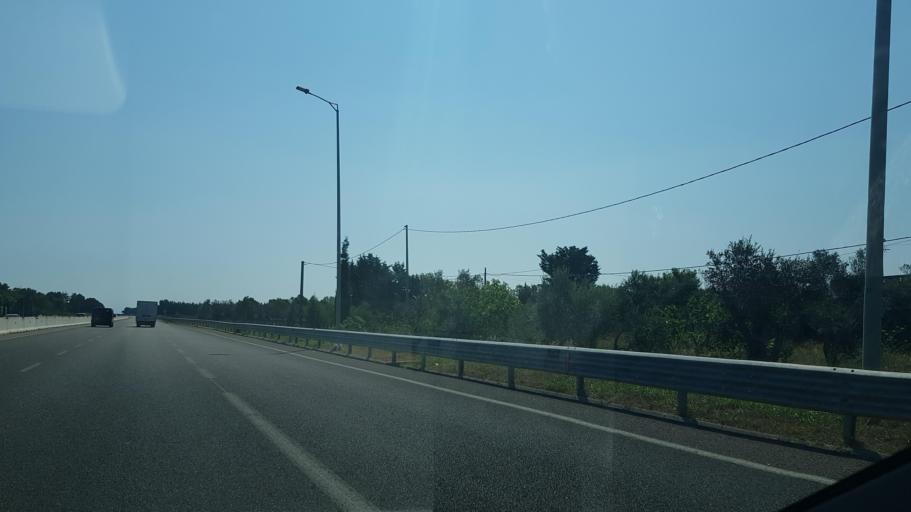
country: IT
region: Apulia
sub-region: Provincia di Lecce
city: Muro Leccese
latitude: 40.1257
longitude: 18.3421
